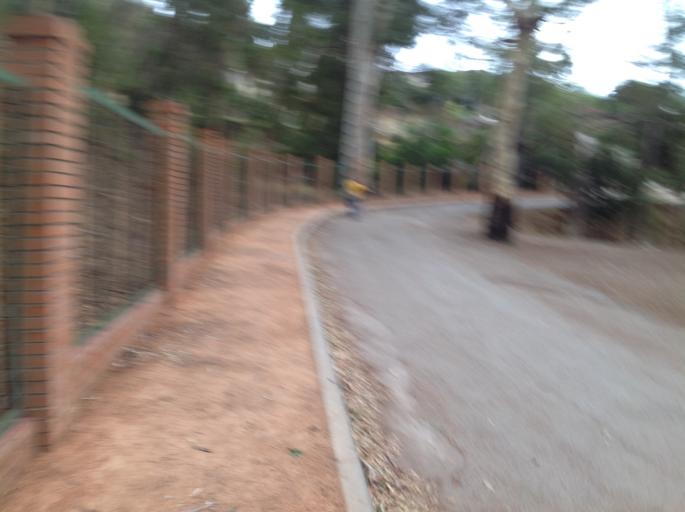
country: ES
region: Andalusia
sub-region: Provincia de Malaga
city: Carratraca
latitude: 36.9108
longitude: -4.7610
